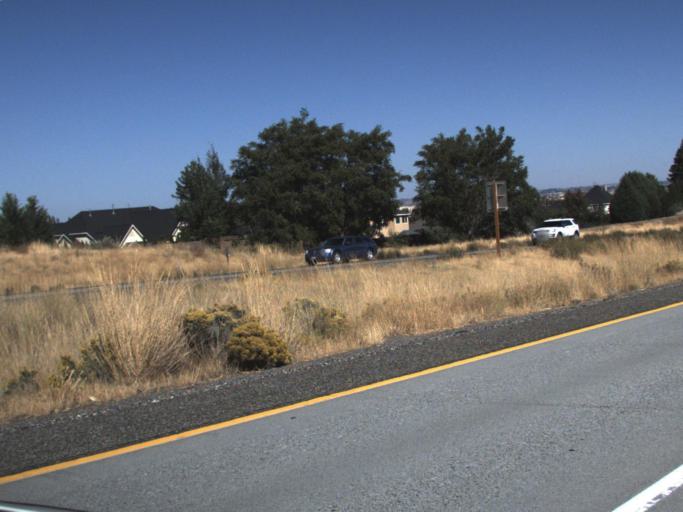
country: US
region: Washington
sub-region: Benton County
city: Richland
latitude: 46.2486
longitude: -119.3221
